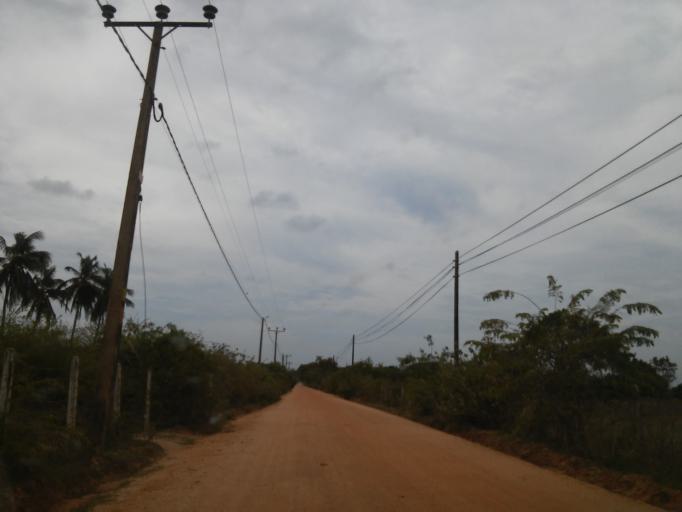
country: LK
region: Eastern Province
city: Trincomalee
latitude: 8.7043
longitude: 81.1812
